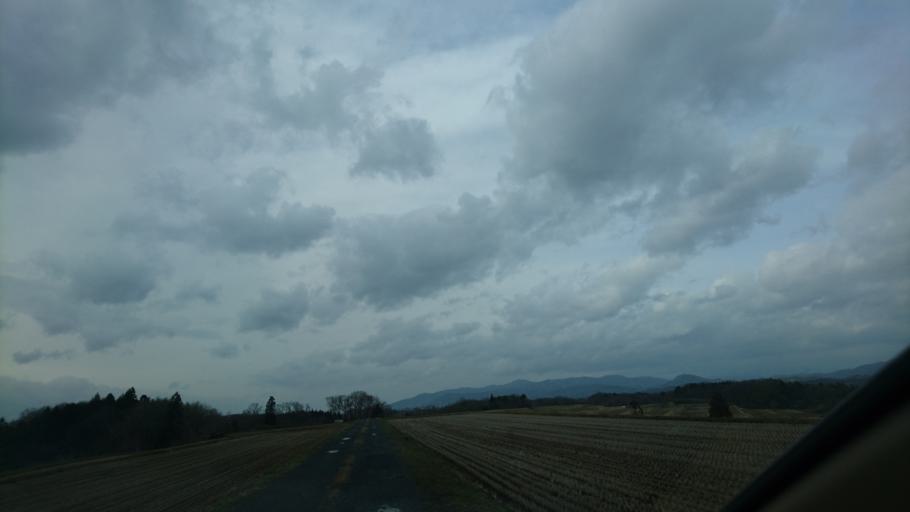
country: JP
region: Iwate
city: Ichinoseki
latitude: 38.8861
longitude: 141.1608
